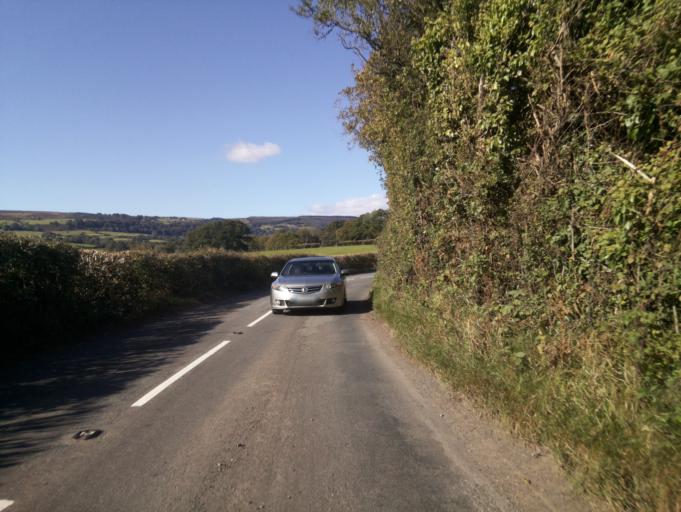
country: GB
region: Wales
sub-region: Torfaen County Borough
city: Cwmbran
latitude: 51.6103
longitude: -3.0492
